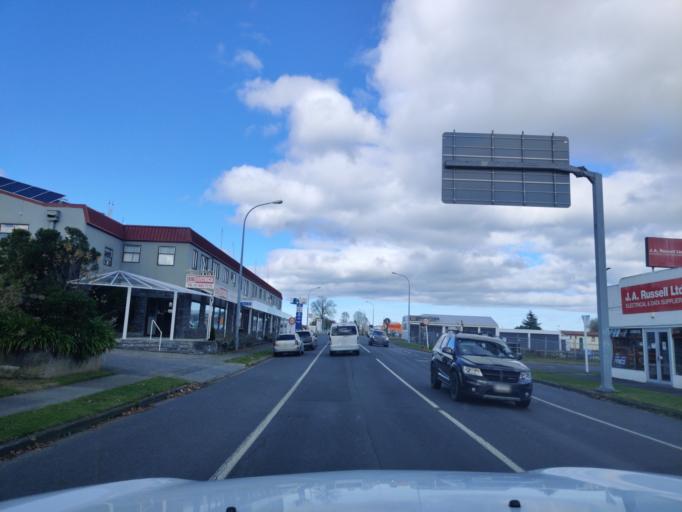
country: NZ
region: Waikato
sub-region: Matamata-Piako District
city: Matamata
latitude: -37.8096
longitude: 175.7706
